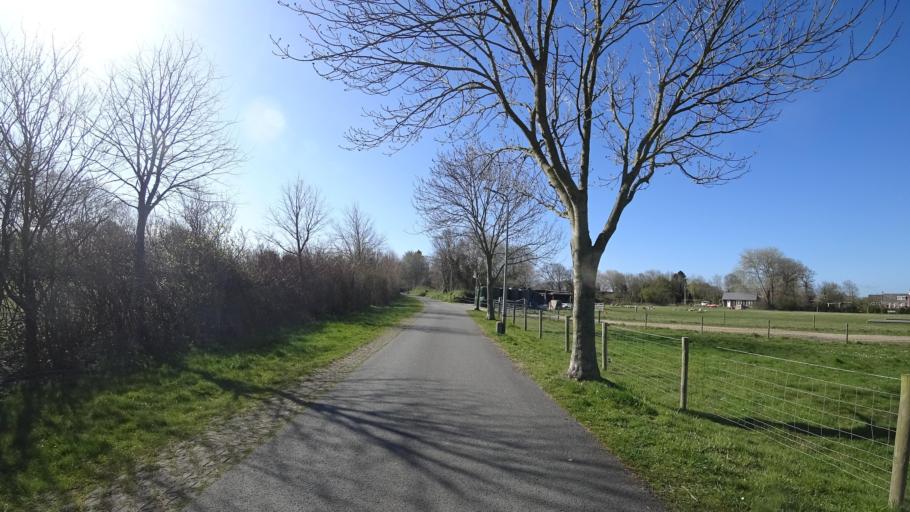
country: NL
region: South Holland
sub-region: Gemeente Goeree-Overflakkee
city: Ouddorp
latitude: 51.8158
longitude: 3.9130
